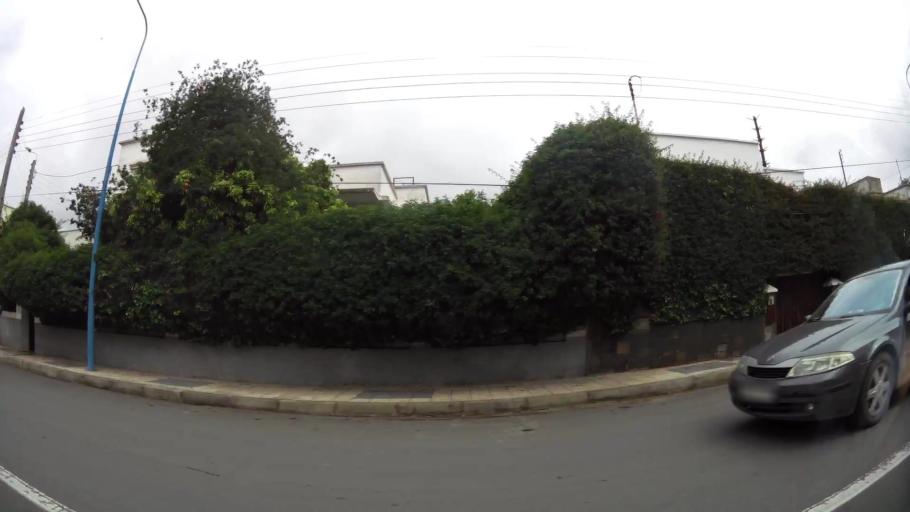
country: MA
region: Grand Casablanca
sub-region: Casablanca
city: Casablanca
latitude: 33.5761
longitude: -7.6123
